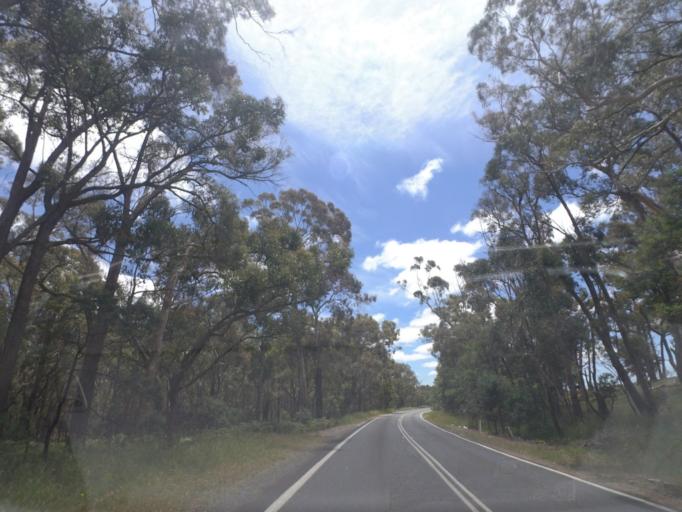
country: AU
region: Victoria
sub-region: Mount Alexander
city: Castlemaine
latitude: -37.3243
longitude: 144.1629
